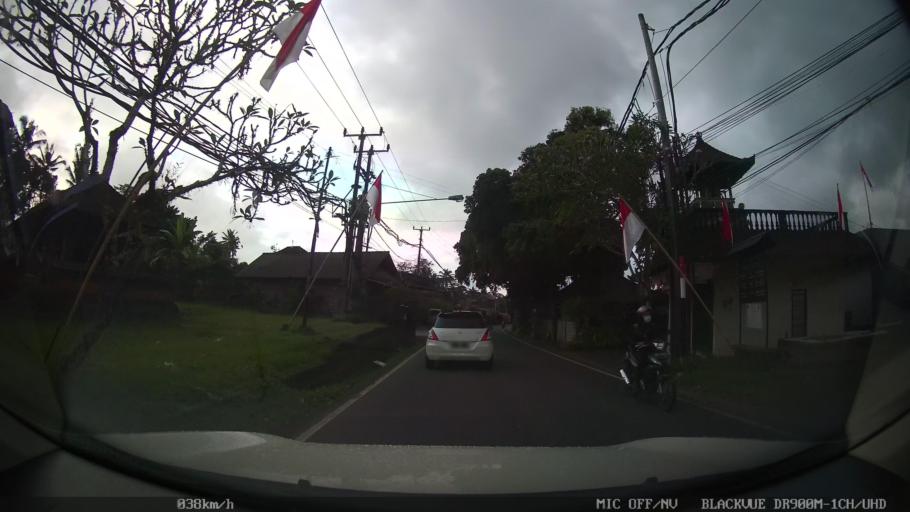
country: ID
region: Bali
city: Bunutan
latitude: -8.4600
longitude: 115.2463
